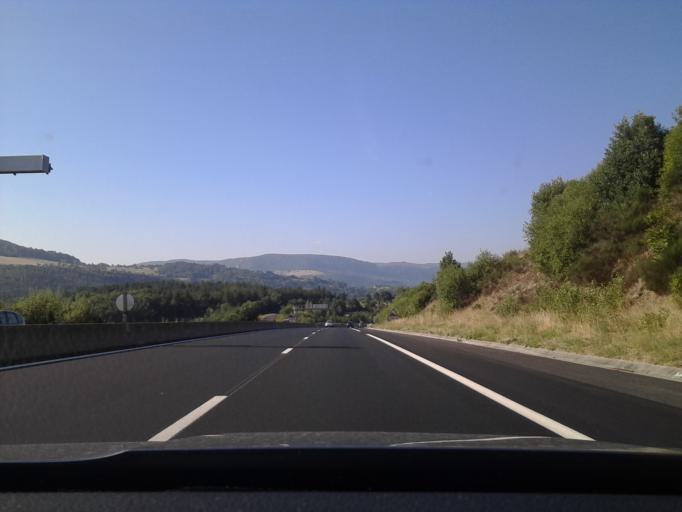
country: FR
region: Languedoc-Roussillon
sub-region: Departement de la Lozere
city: La Canourgue
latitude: 44.4767
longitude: 3.1982
